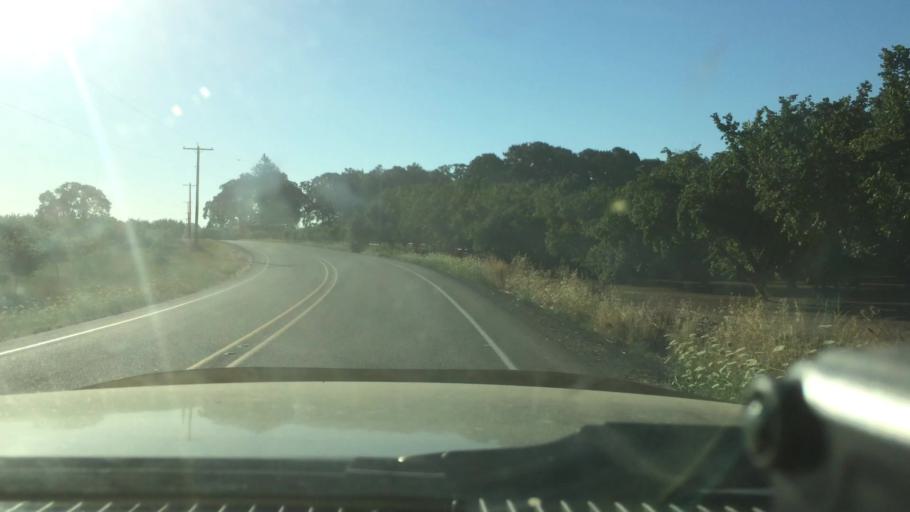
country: US
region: Oregon
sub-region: Marion County
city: Gervais
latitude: 45.1157
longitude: -122.9758
